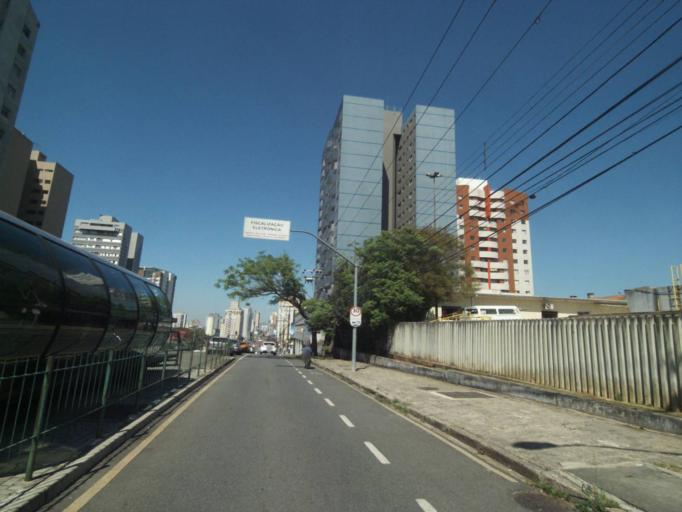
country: BR
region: Parana
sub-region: Curitiba
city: Curitiba
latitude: -25.3995
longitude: -49.2462
